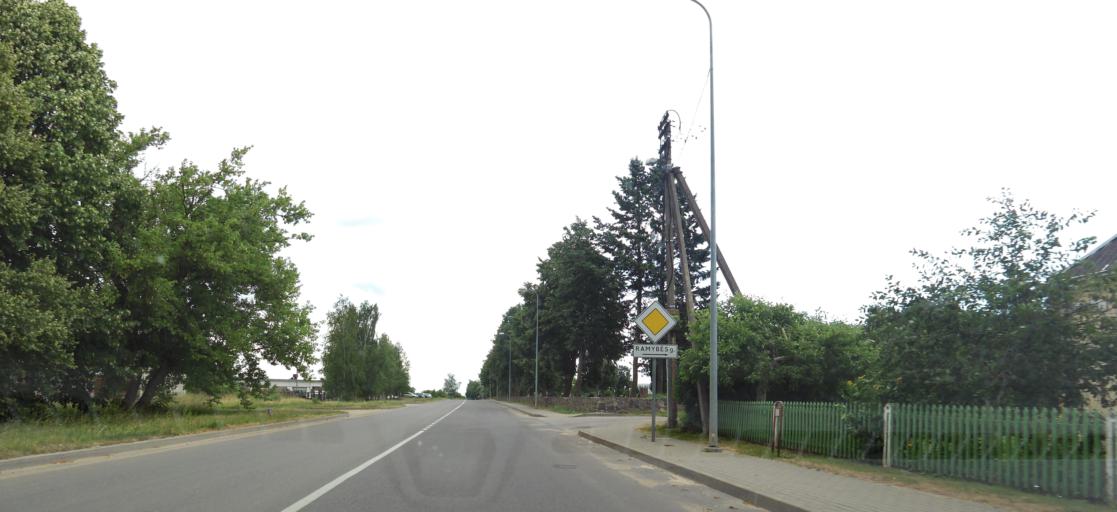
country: LT
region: Vilnius County
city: Ukmerge
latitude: 55.2596
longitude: 24.7722
